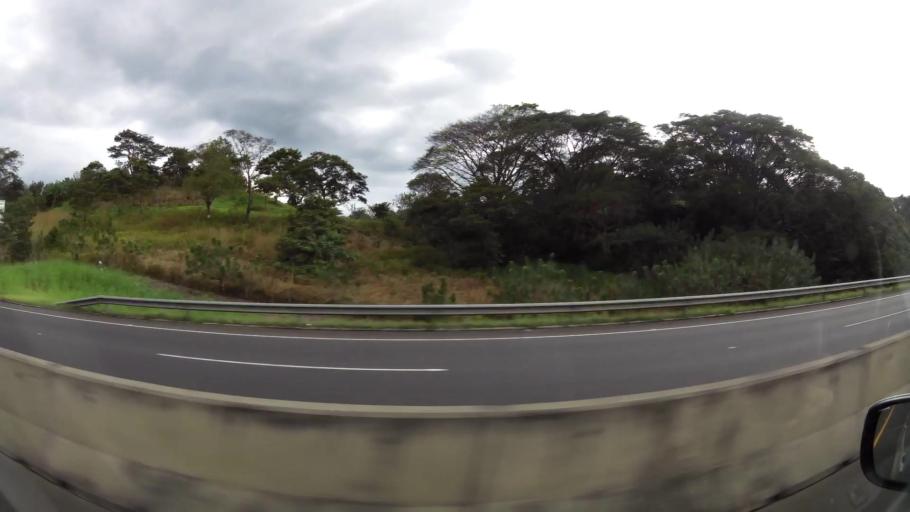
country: CR
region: Alajuela
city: Atenas
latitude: 9.9536
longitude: -84.3600
